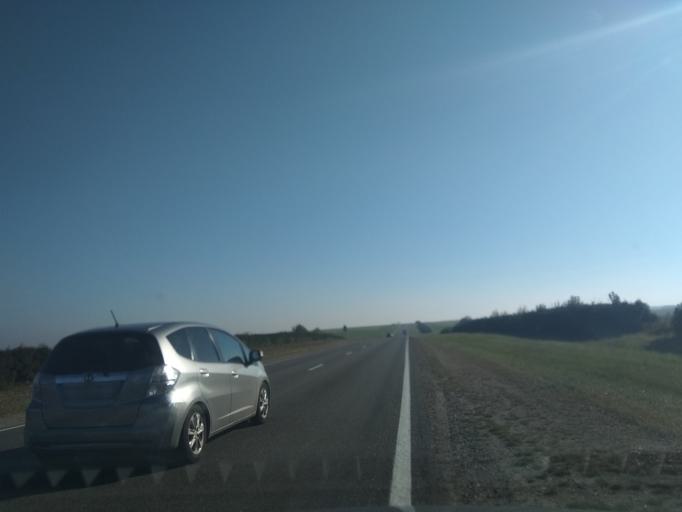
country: BY
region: Grodnenskaya
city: Zel'va
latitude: 53.1367
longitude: 24.9527
